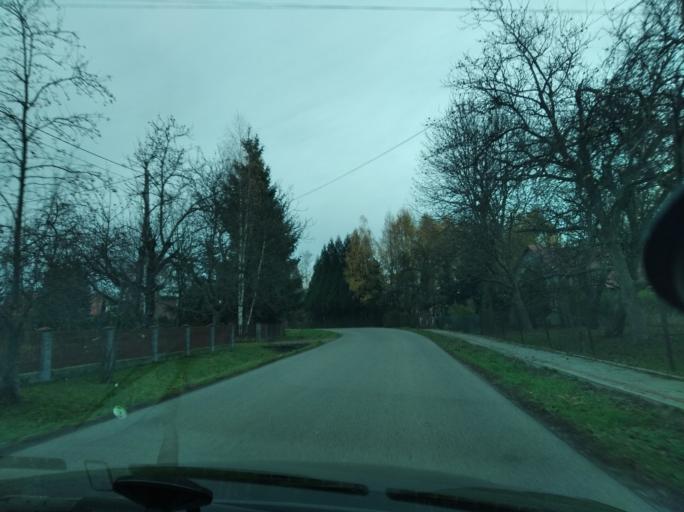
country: PL
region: Subcarpathian Voivodeship
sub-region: Powiat lancucki
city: Lancut
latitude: 50.0963
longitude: 22.2205
